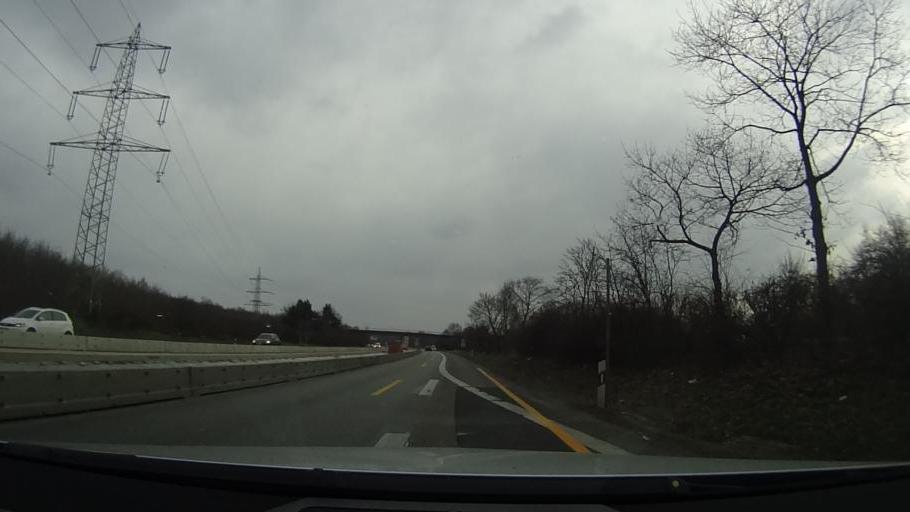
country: DE
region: Hesse
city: Kelsterbach
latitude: 50.0591
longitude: 8.5490
